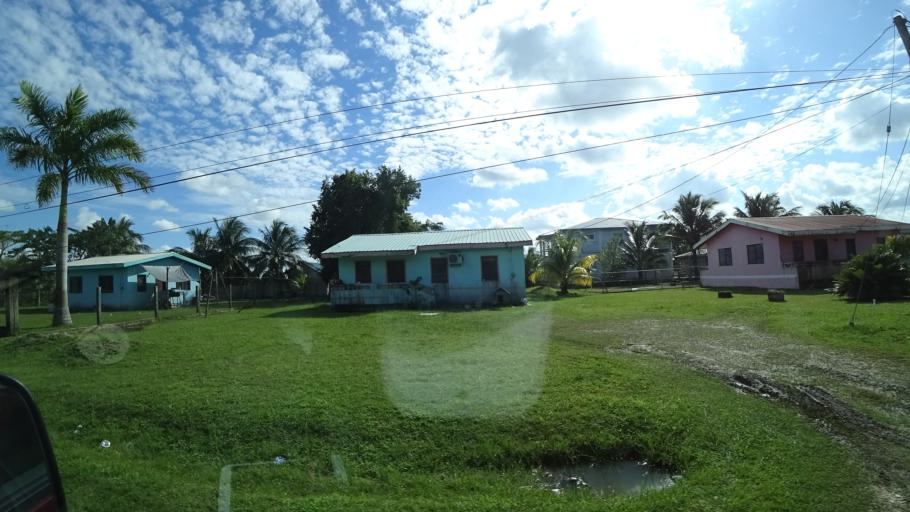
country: BZ
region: Belize
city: Belize City
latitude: 17.5691
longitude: -88.4153
